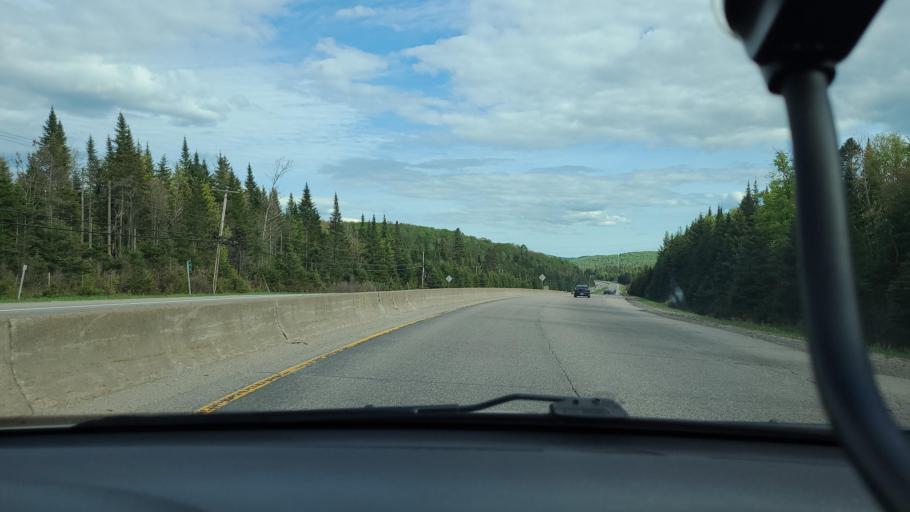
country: CA
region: Quebec
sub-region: Laurentides
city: Sainte-Agathe-des-Monts
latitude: 46.0876
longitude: -74.3255
